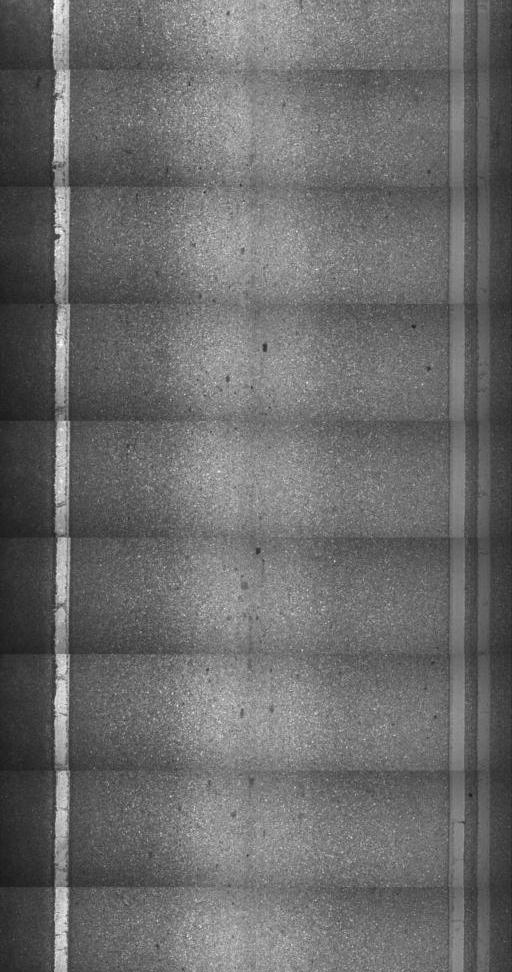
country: US
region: Vermont
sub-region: Rutland County
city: Brandon
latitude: 43.8669
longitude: -73.1998
